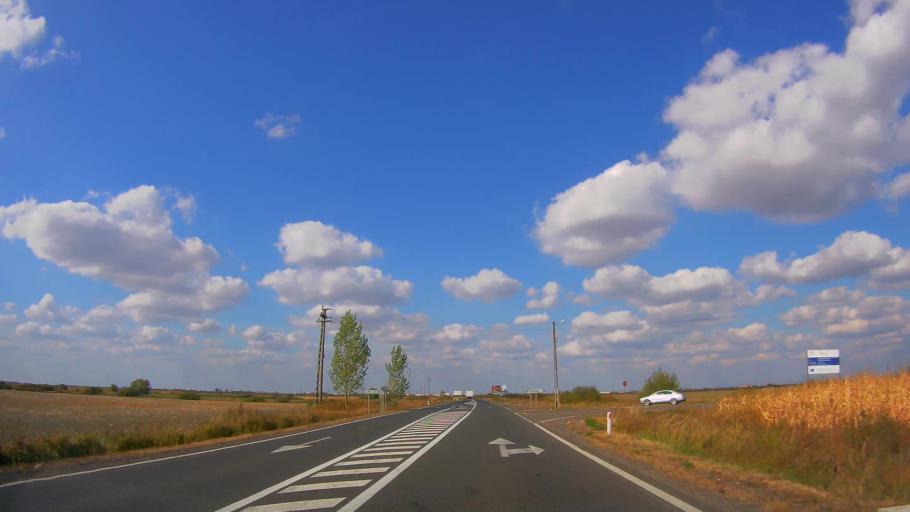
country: RO
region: Satu Mare
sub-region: Oras Ardud
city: Madaras
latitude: 47.7076
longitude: 22.8724
